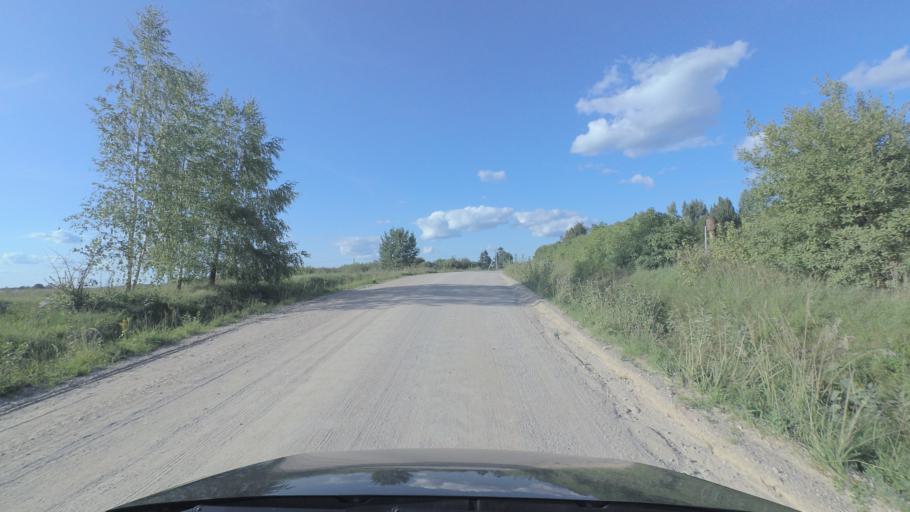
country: LT
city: Pabrade
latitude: 55.1279
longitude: 25.7049
